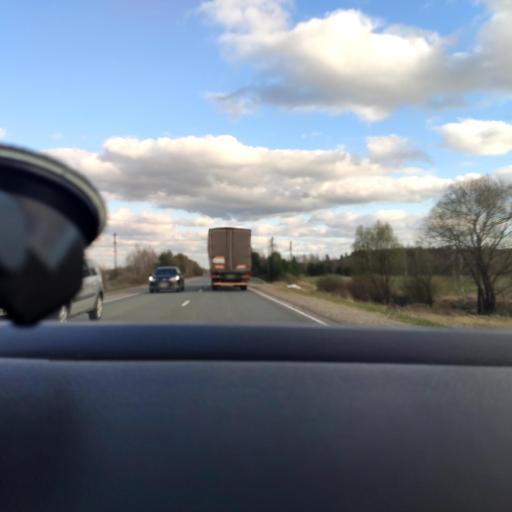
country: RU
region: Moskovskaya
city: Yegor'yevsk
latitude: 55.4226
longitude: 39.0385
